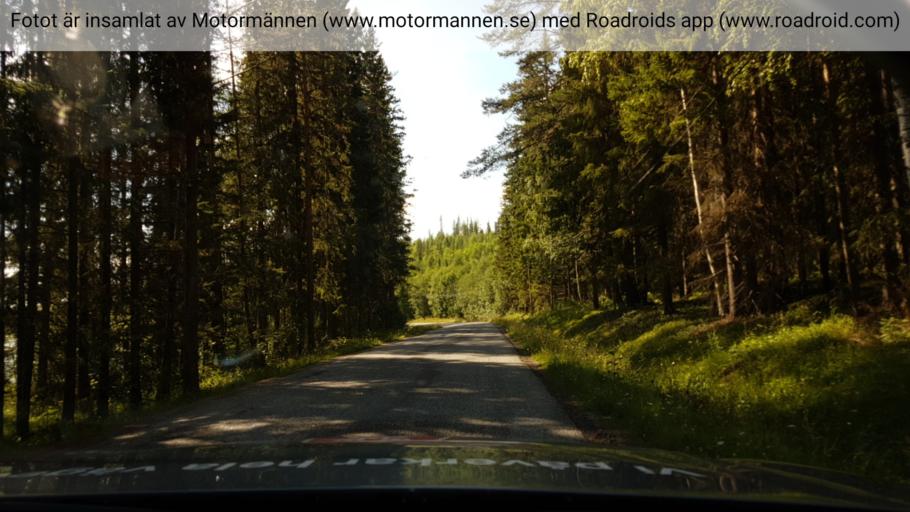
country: SE
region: Vaesterbotten
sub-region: Dorotea Kommun
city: Dorotea
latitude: 64.1292
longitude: 16.2376
